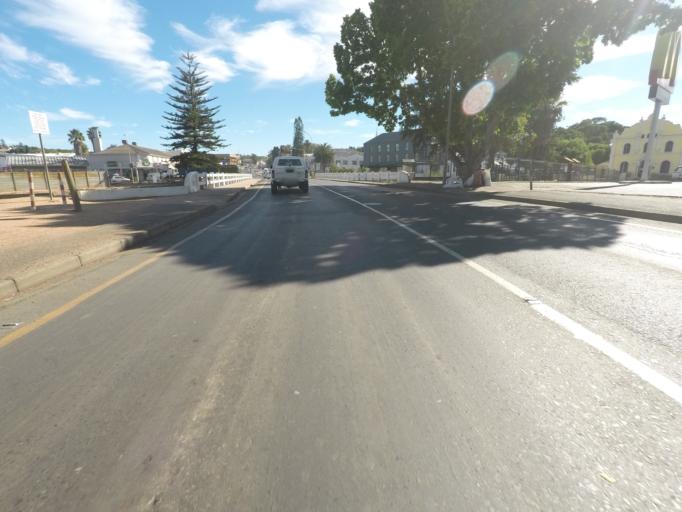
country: ZA
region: Western Cape
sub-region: West Coast District Municipality
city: Malmesbury
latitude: -33.4667
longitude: 18.7289
